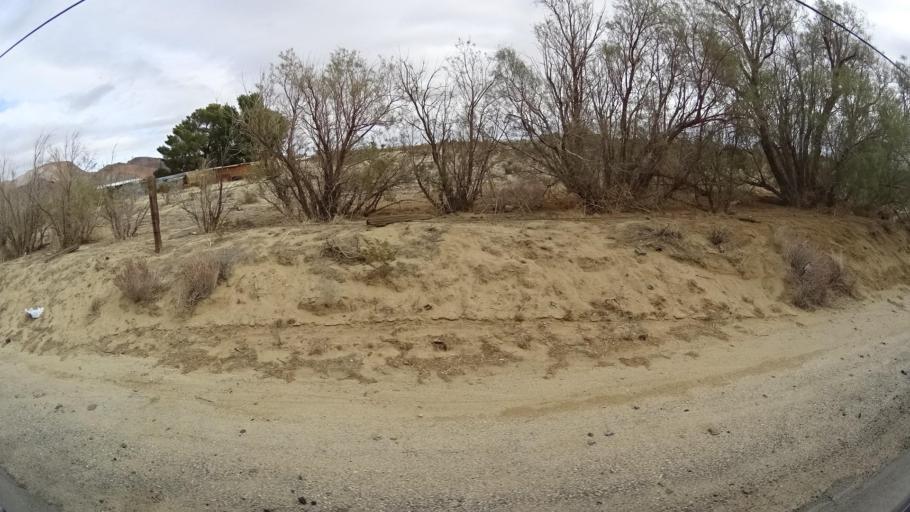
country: US
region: California
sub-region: Kern County
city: Rosamond
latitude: 34.9495
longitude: -118.2126
